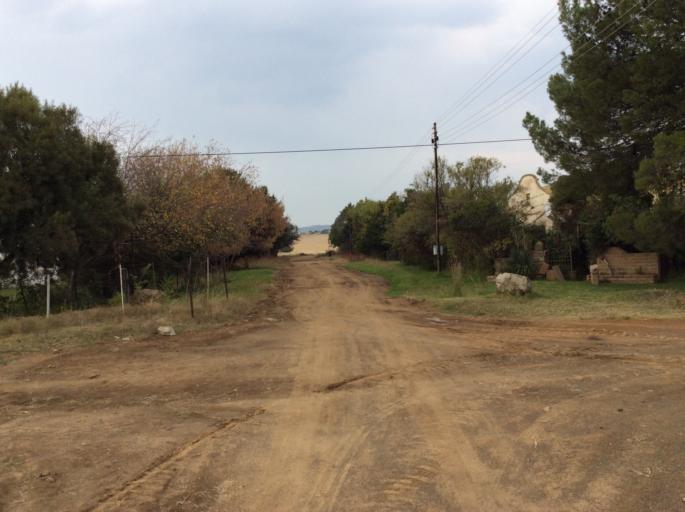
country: LS
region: Mafeteng
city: Mafeteng
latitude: -29.9882
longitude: 27.0177
